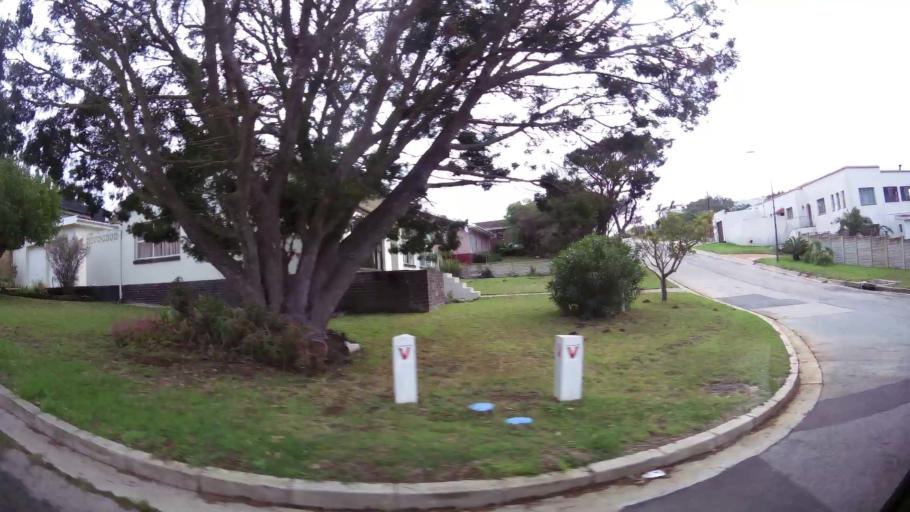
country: ZA
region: Eastern Cape
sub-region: Nelson Mandela Bay Metropolitan Municipality
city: Port Elizabeth
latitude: -33.9325
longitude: 25.5200
